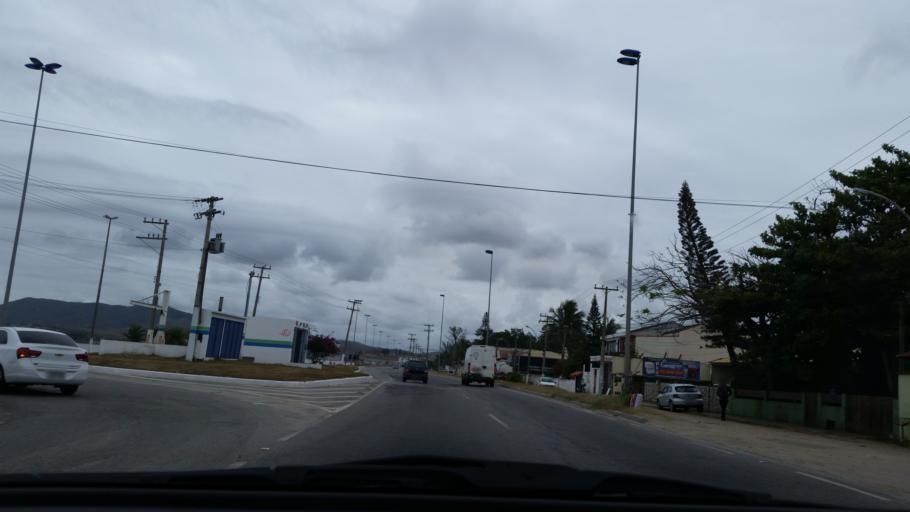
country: BR
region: Rio de Janeiro
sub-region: Sao Pedro Da Aldeia
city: Sao Pedro da Aldeia
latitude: -22.8320
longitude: -42.1056
